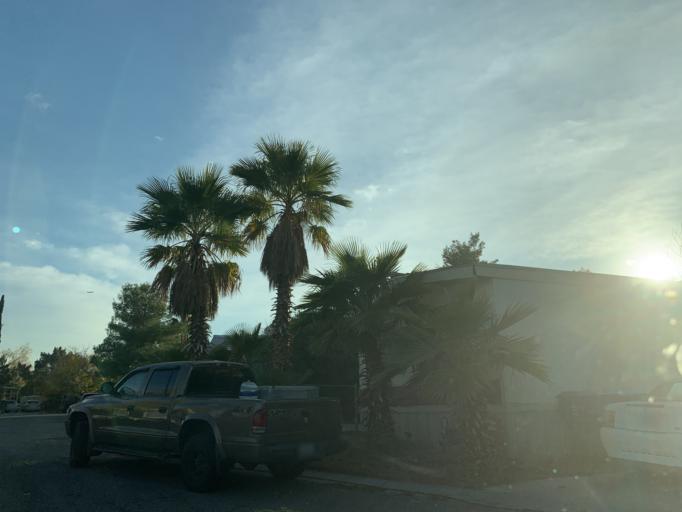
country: US
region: Nevada
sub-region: Clark County
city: Spring Valley
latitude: 36.1037
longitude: -115.2172
